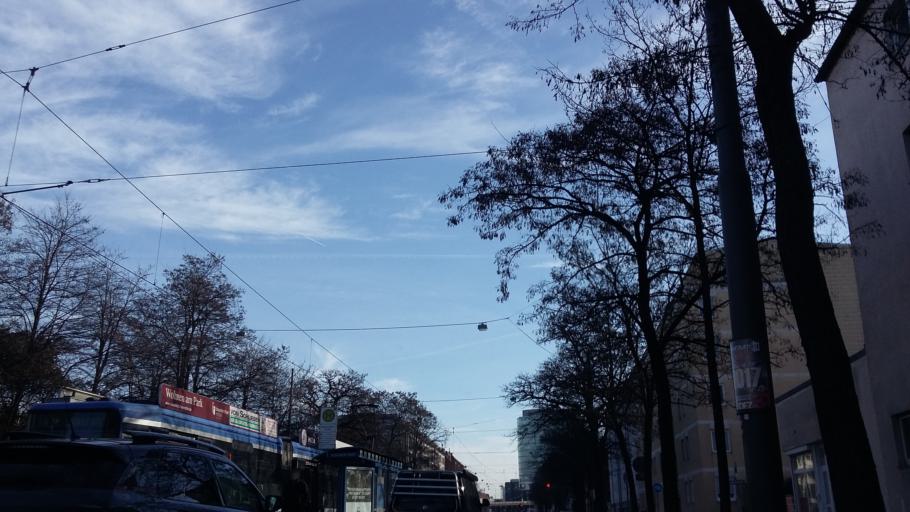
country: DE
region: Bavaria
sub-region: Upper Bavaria
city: Munich
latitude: 48.1472
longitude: 11.5292
